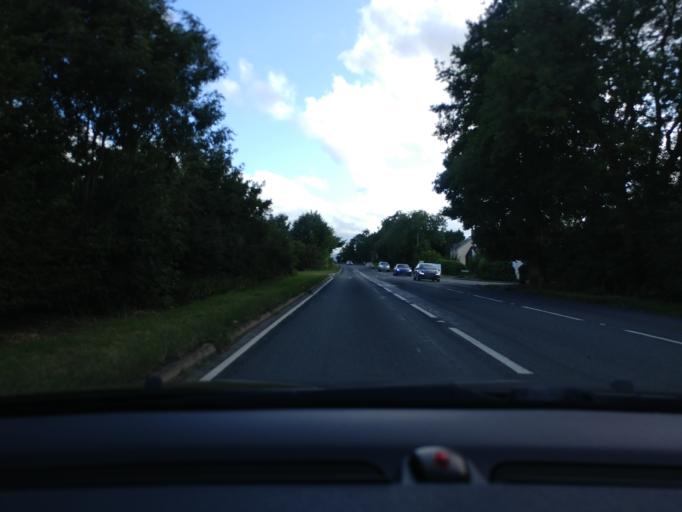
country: GB
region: England
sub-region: Oxfordshire
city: Bicester
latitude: 51.8795
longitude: -1.2300
